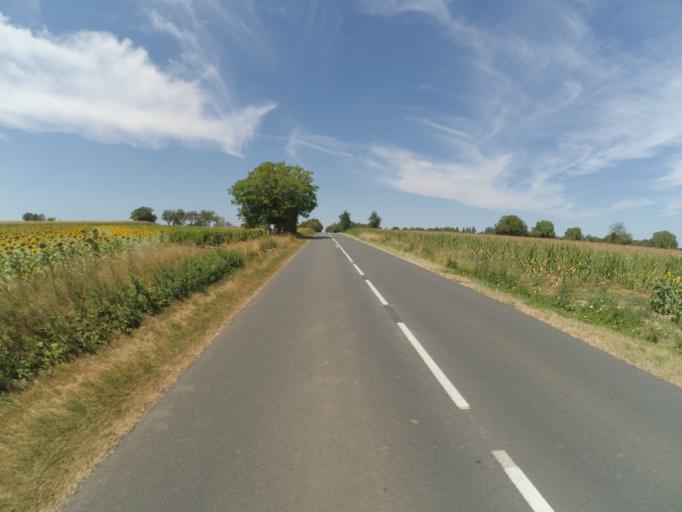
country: FR
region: Poitou-Charentes
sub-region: Departement de la Vienne
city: Usson-du-Poitou
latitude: 46.2958
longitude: 0.5062
